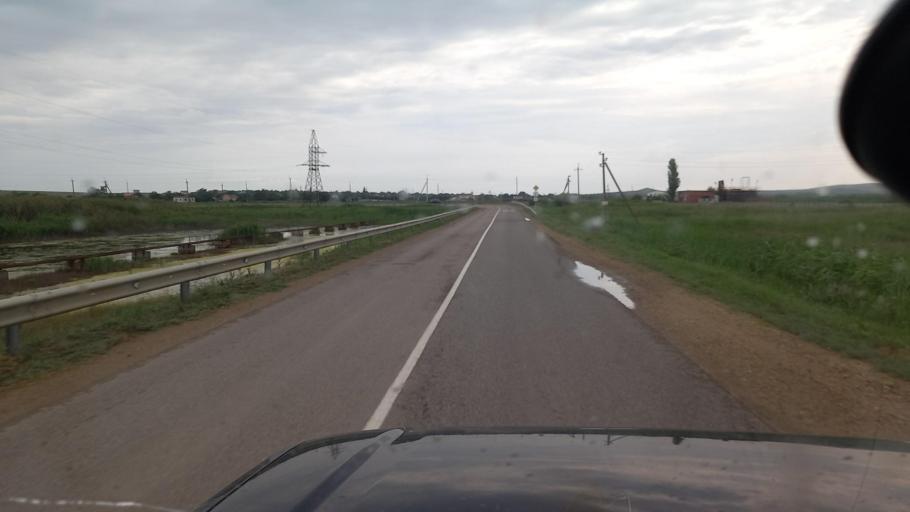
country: RU
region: Krasnodarskiy
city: Akhtanizovskaya
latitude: 45.3393
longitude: 37.1160
